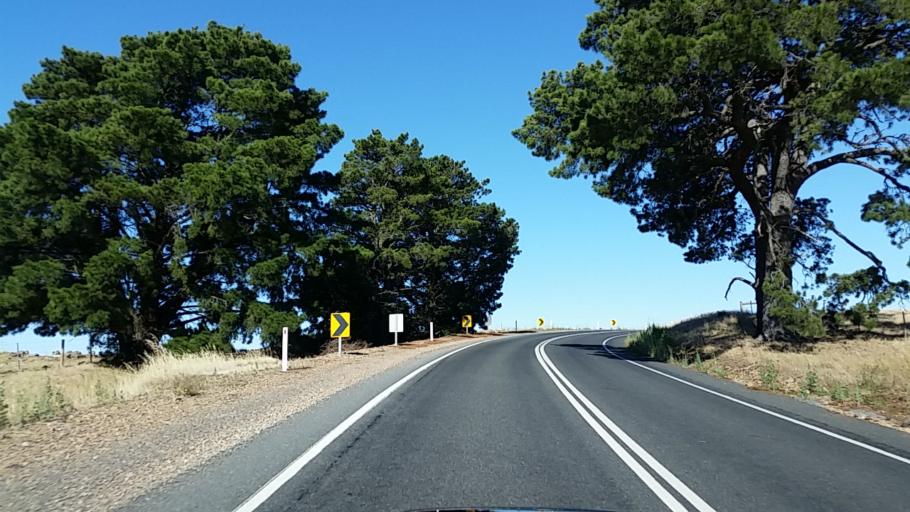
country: AU
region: South Australia
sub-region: Adelaide Hills
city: Birdwood
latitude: -34.7710
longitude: 139.1110
